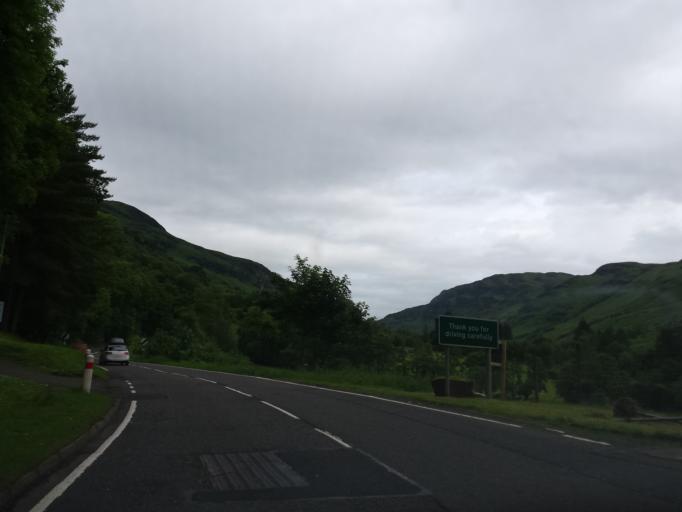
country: GB
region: Scotland
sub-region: Stirling
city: Callander
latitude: 56.3873
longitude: -4.2889
